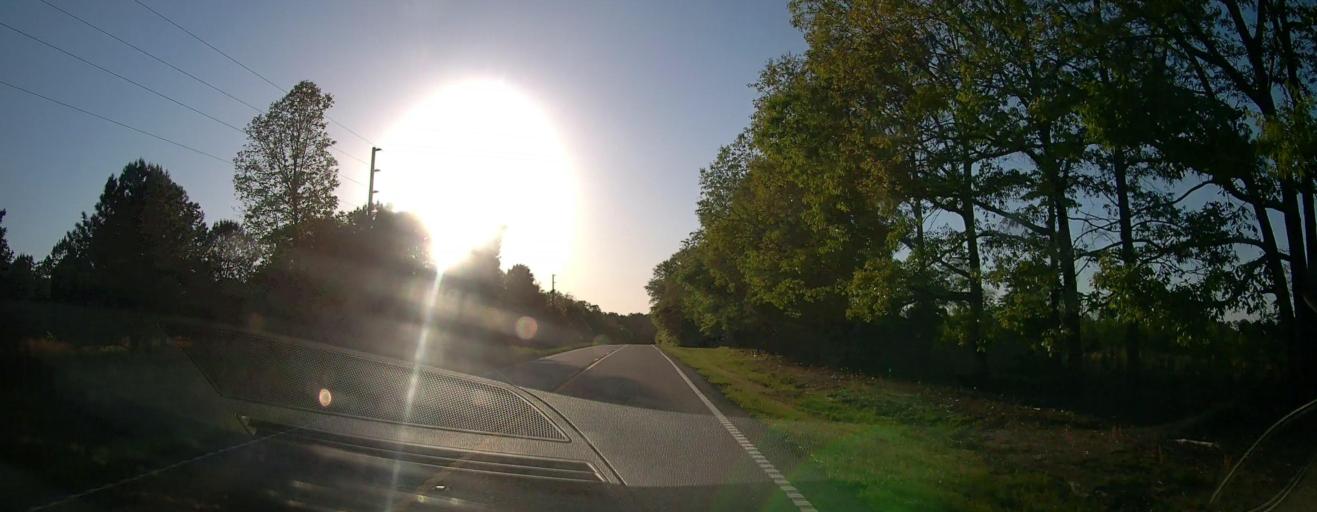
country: US
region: Georgia
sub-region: Schley County
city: Ellaville
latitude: 32.3319
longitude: -84.3438
